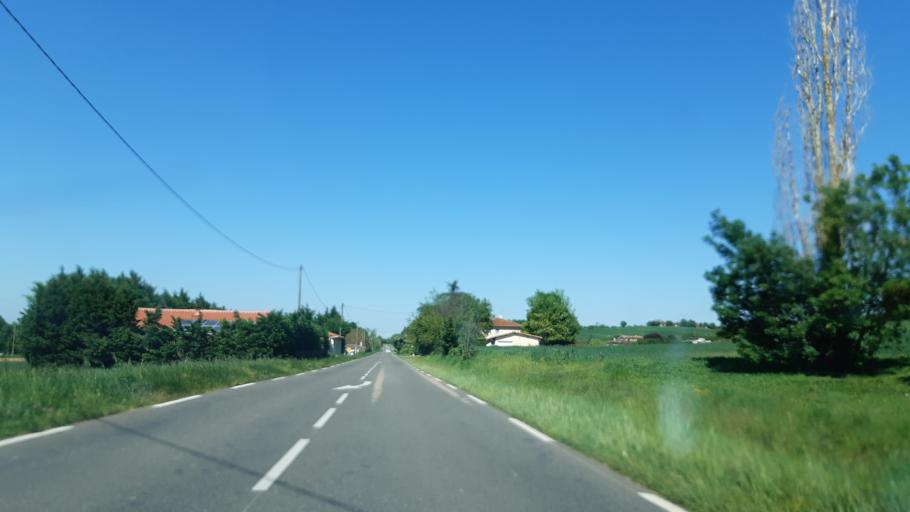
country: FR
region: Midi-Pyrenees
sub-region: Departement du Gers
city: Pujaudran
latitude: 43.5838
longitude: 1.0477
